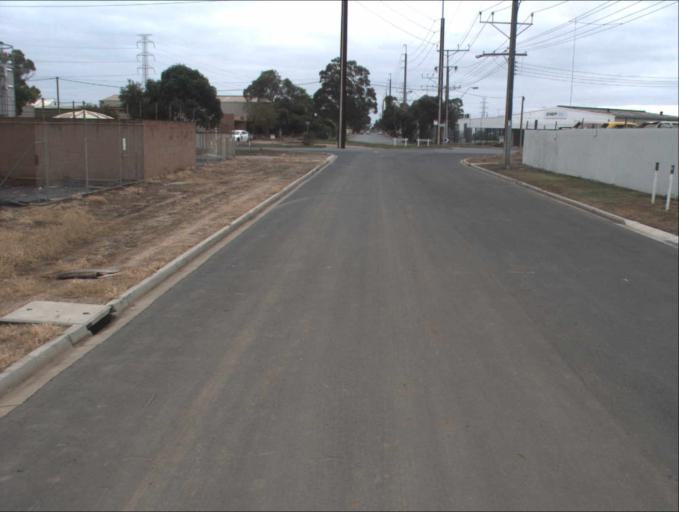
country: AU
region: South Australia
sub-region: Port Adelaide Enfield
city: Blair Athol
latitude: -34.8477
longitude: 138.5823
